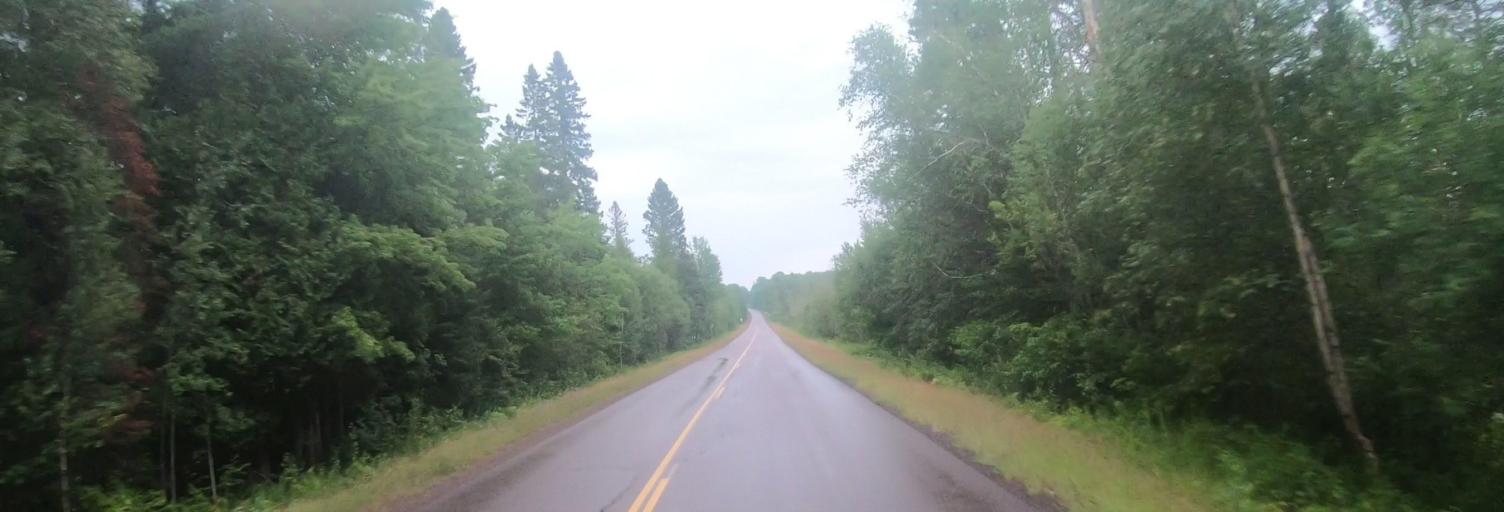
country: US
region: Michigan
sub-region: Keweenaw County
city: Eagle River
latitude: 47.2851
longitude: -88.2821
